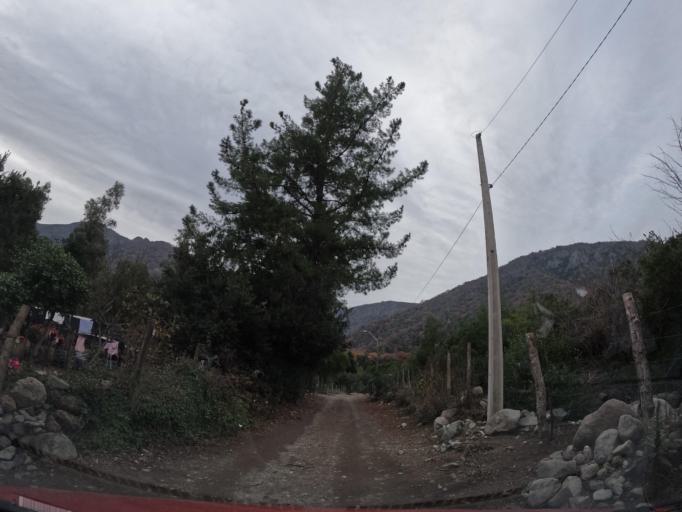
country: CL
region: Maule
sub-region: Provincia de Linares
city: Colbun
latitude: -35.7245
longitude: -71.0187
